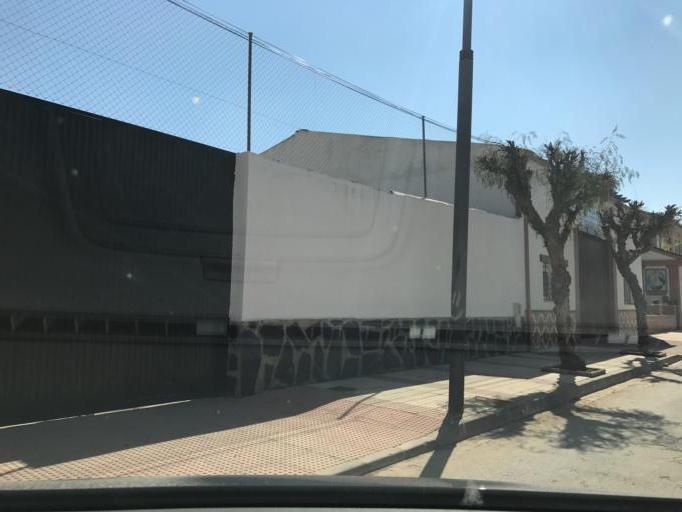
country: ES
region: Andalusia
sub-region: Provincia de Granada
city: Chauchina
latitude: 37.1948
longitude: -3.7736
